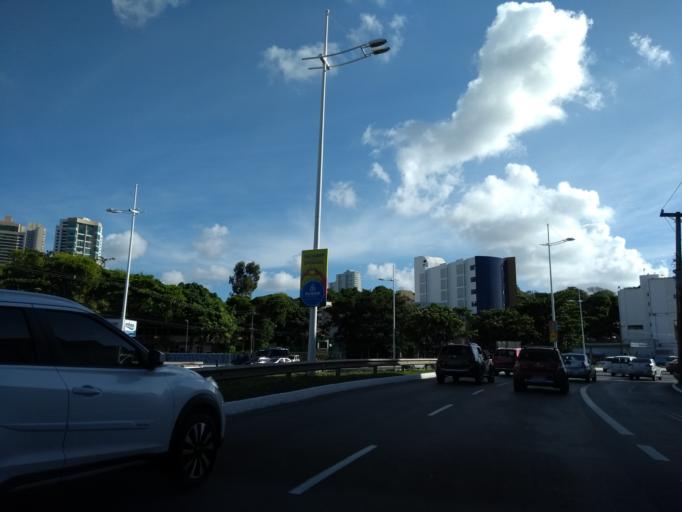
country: BR
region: Bahia
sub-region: Salvador
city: Salvador
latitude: -13.0060
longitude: -38.4869
